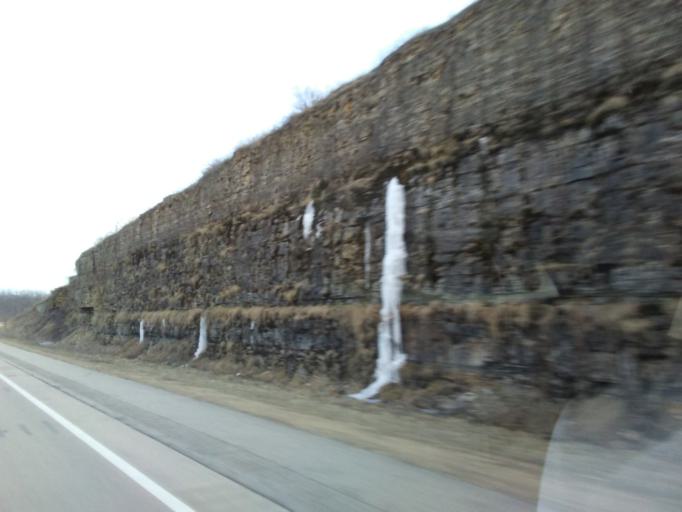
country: US
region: Wisconsin
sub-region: Iowa County
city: Barneveld
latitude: 43.0104
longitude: -89.8834
